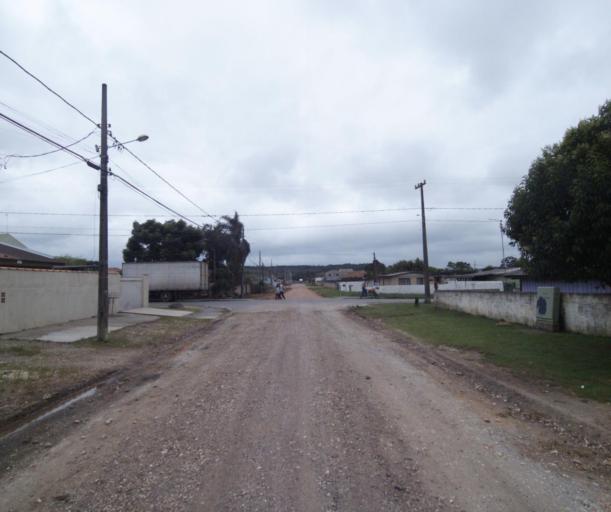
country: BR
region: Parana
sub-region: Quatro Barras
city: Quatro Barras
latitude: -25.3609
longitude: -49.0969
